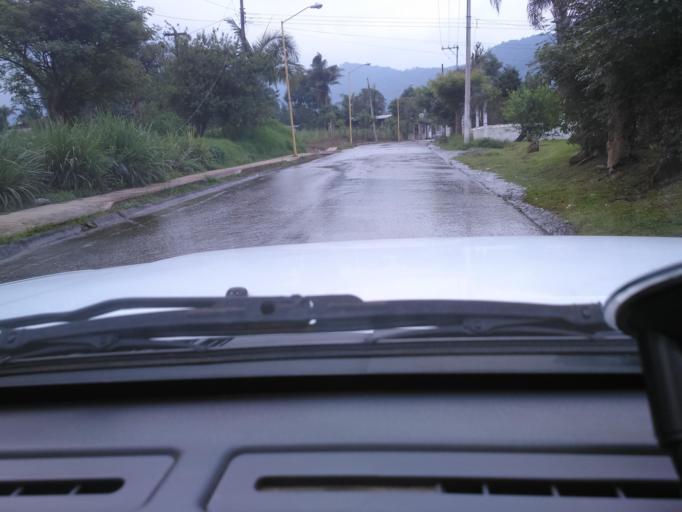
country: MX
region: Veracruz
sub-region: Mariano Escobedo
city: Chicola
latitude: 18.8975
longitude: -97.1079
